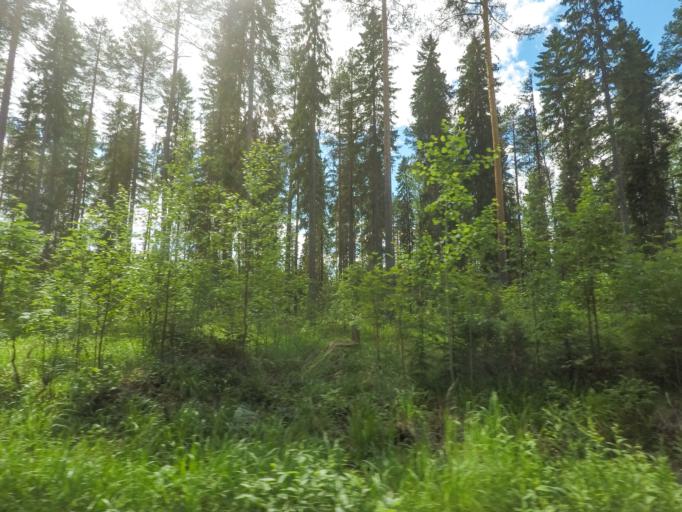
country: FI
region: Central Finland
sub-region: Jyvaeskylae
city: Hankasalmi
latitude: 62.4075
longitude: 26.6522
